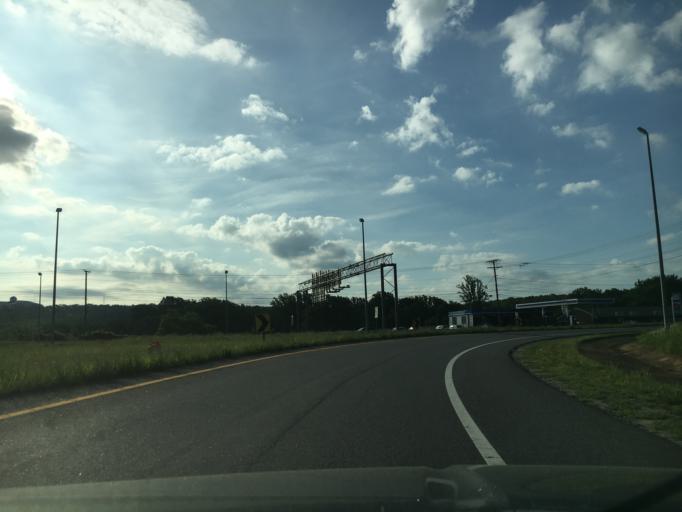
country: US
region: Virginia
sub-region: Campbell County
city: Timberlake
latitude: 37.3374
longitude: -79.1923
